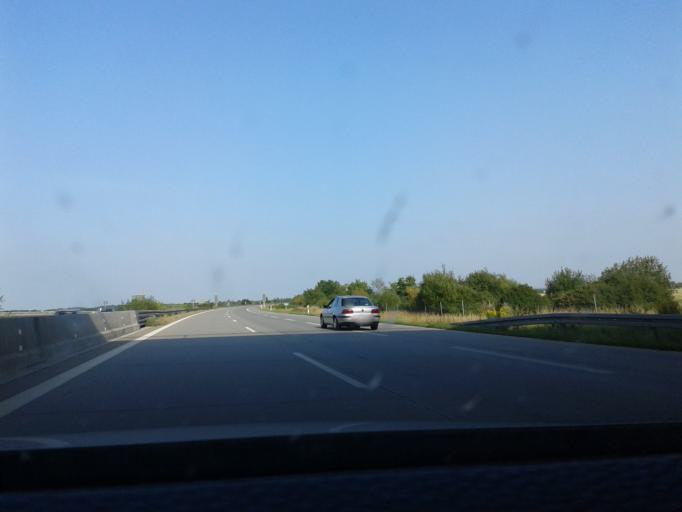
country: DE
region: Saxony
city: Kitzen
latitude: 51.2631
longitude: 12.2690
